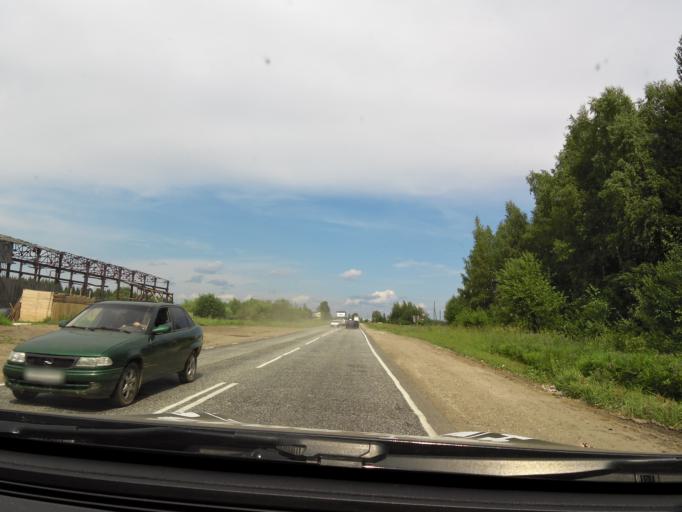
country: RU
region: Kirov
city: Vakhrushi
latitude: 58.6669
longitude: 49.9325
